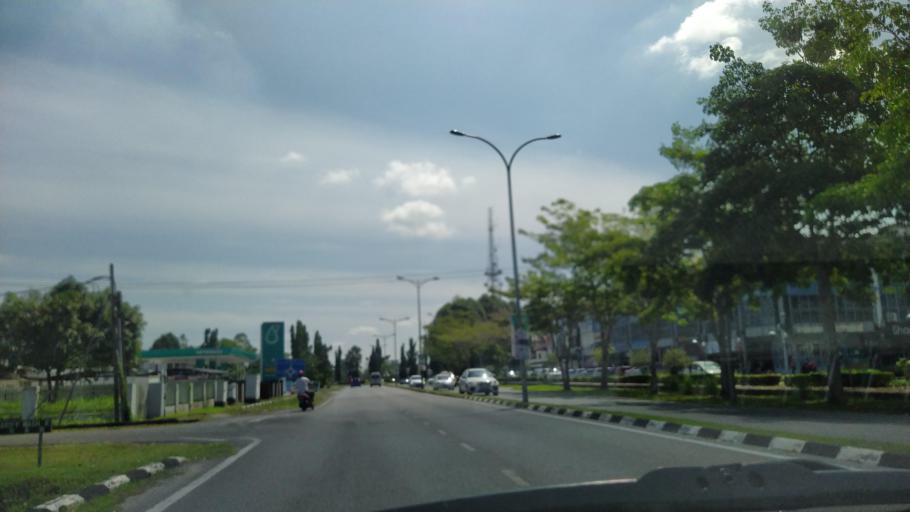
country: MY
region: Sarawak
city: Sibu
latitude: 2.3107
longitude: 111.8301
